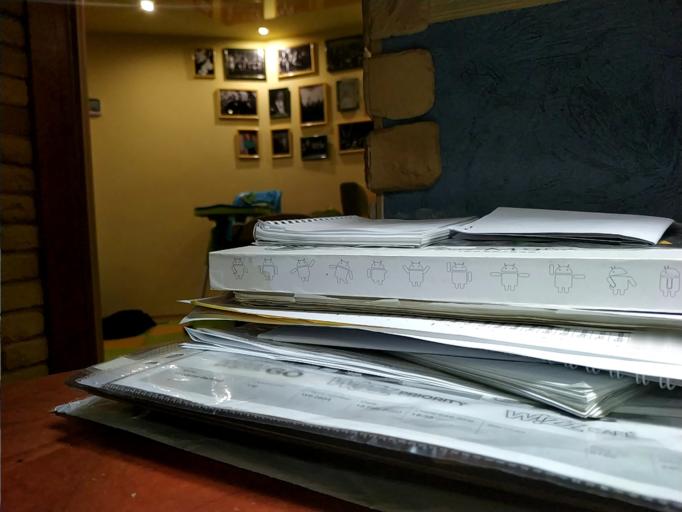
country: RU
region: Arkhangelskaya
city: Kargopol'
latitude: 61.5635
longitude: 39.2859
